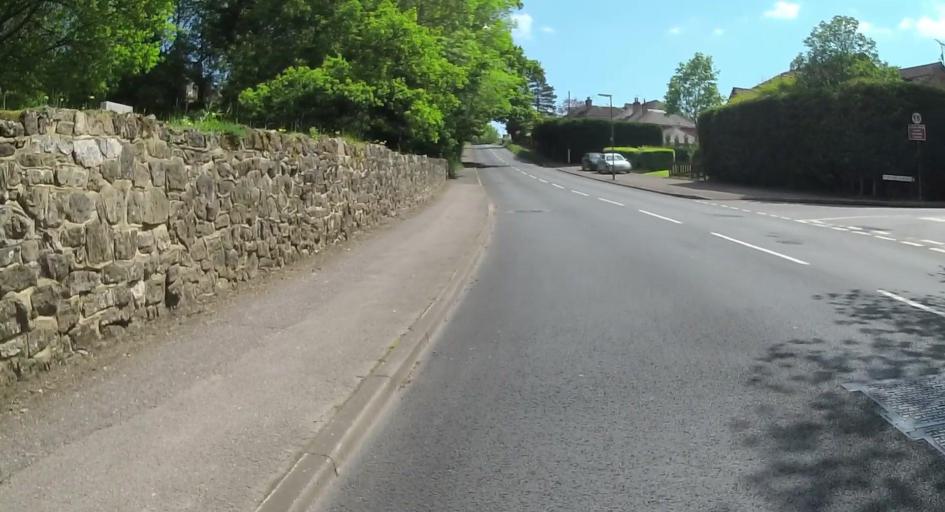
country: GB
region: England
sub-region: Surrey
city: Farnham
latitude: 51.1975
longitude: -0.8174
